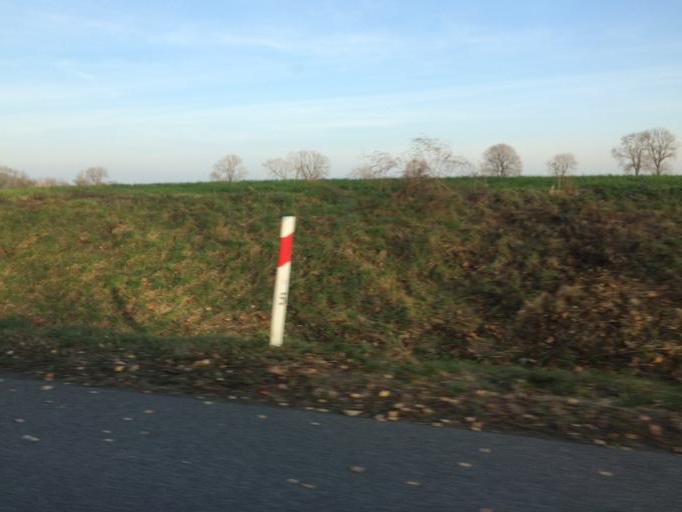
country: PL
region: Opole Voivodeship
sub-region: Powiat strzelecki
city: Strzelce Opolskie
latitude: 50.4978
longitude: 18.3377
